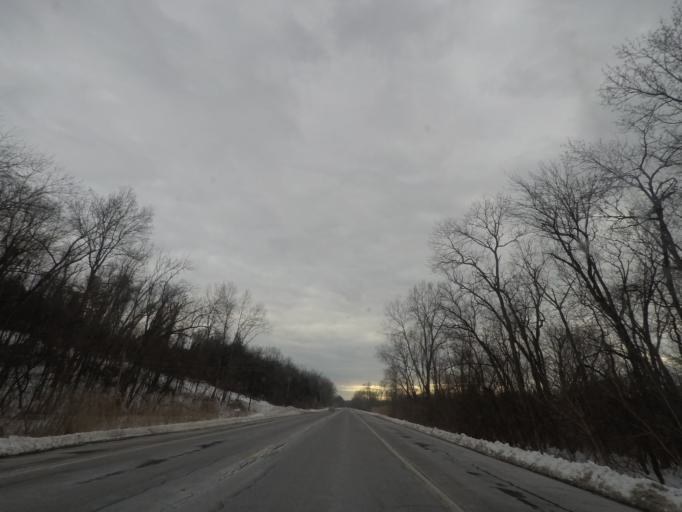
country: US
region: New York
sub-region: Rensselaer County
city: East Greenbush
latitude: 42.5676
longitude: -73.7405
